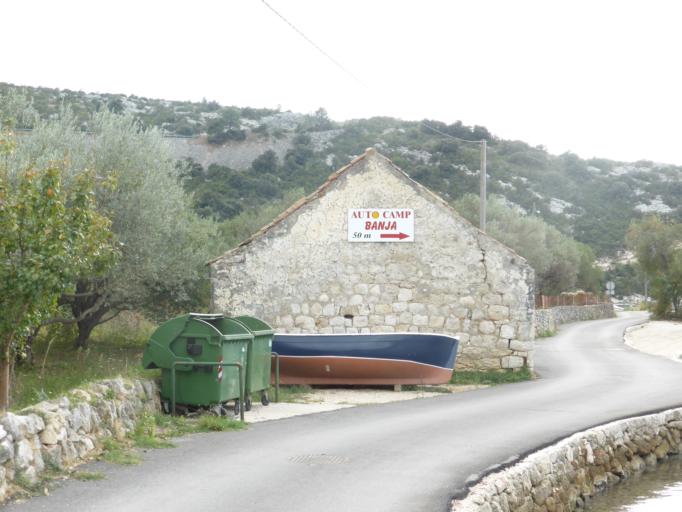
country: HR
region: Dubrovacko-Neretvanska
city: Podgora
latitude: 42.7751
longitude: 17.8848
